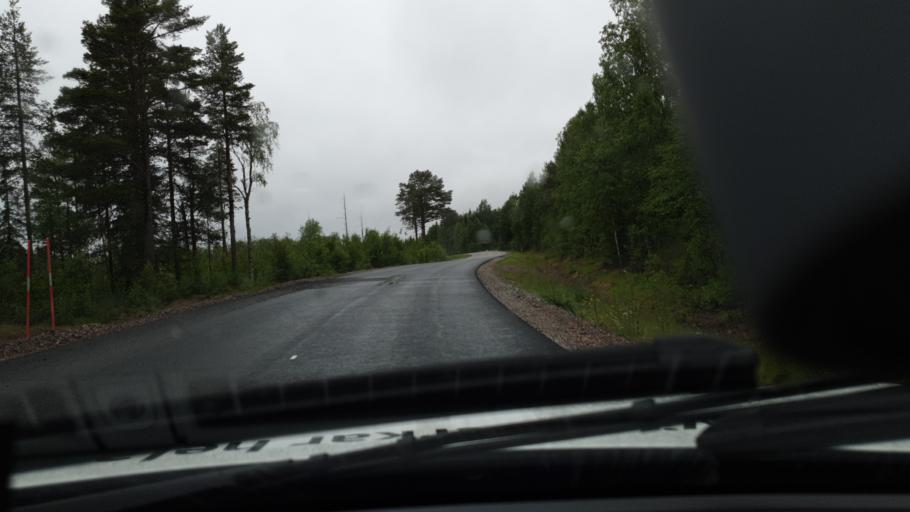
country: SE
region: Norrbotten
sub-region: Overtornea Kommun
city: OEvertornea
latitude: 66.5500
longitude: 23.3423
